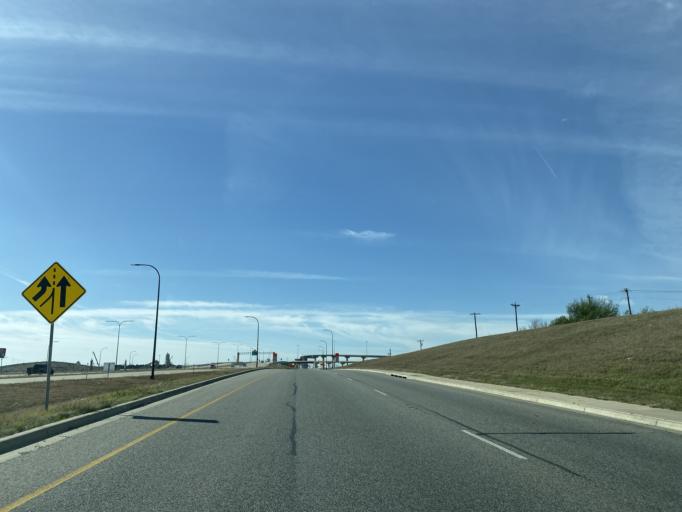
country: US
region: Texas
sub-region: Travis County
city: Manor
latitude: 30.3438
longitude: -97.5840
